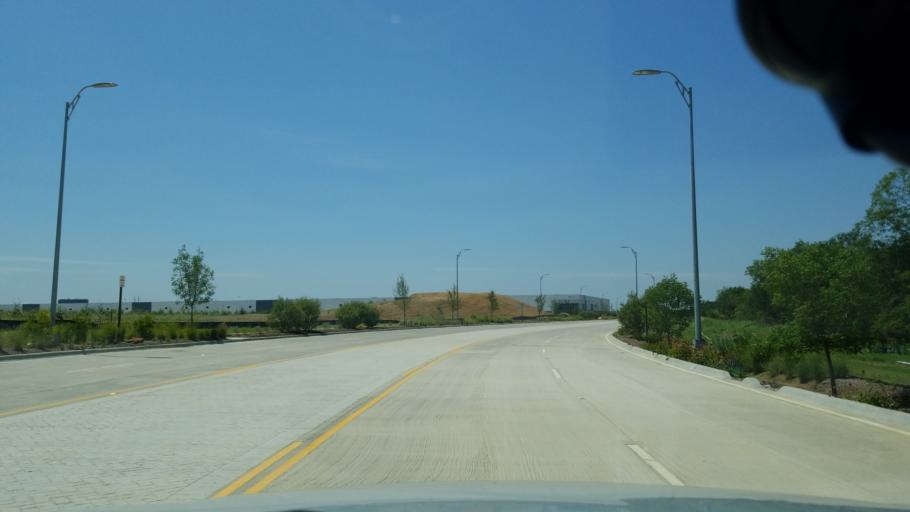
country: US
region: Texas
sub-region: Tarrant County
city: Euless
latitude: 32.8488
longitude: -97.0311
